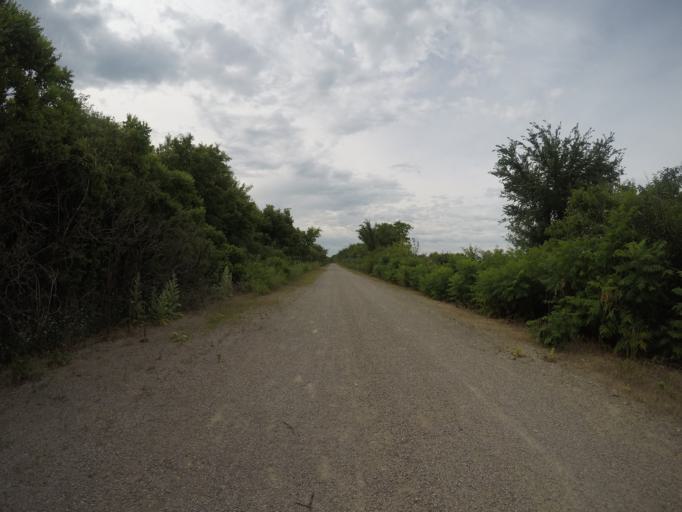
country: US
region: Kansas
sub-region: Anderson County
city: Garnett
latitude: 38.4240
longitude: -95.2631
